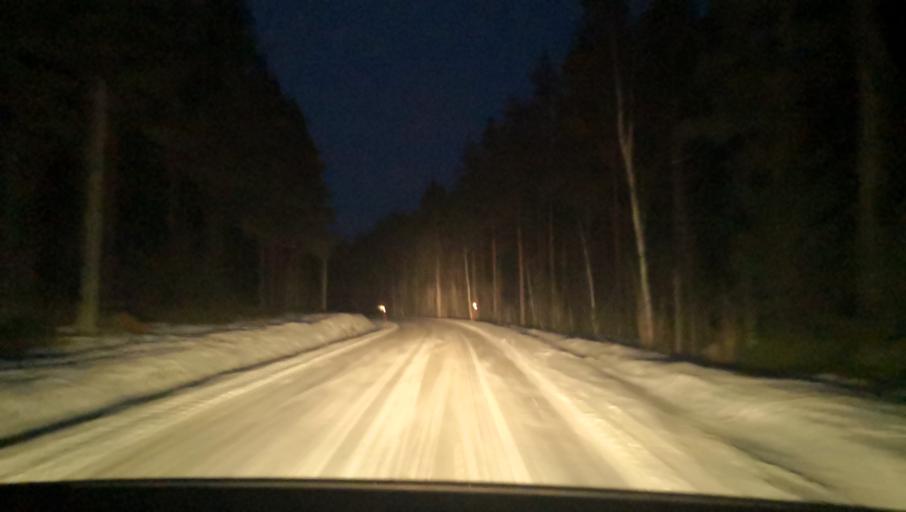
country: SE
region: Uppsala
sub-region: Heby Kommun
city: Tarnsjo
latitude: 60.2873
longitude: 16.8069
